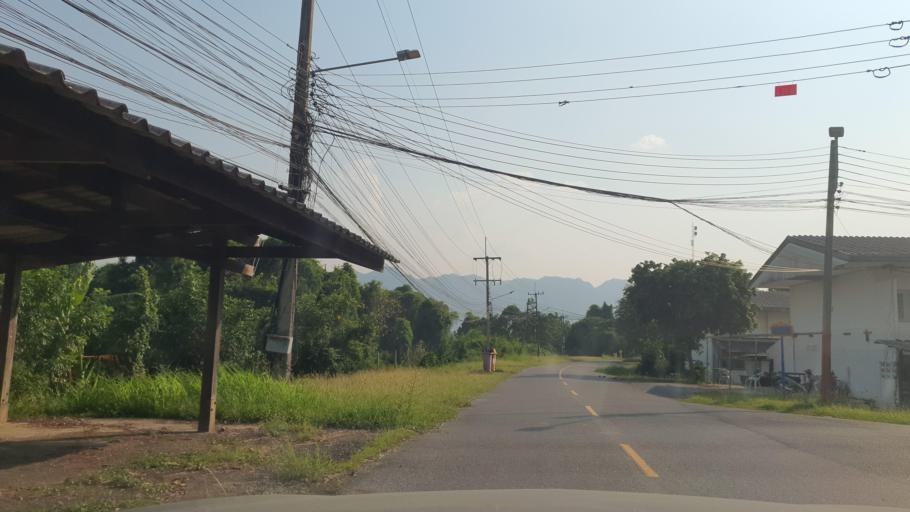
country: TH
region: Kanchanaburi
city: Sai Yok
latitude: 14.2262
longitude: 99.2339
